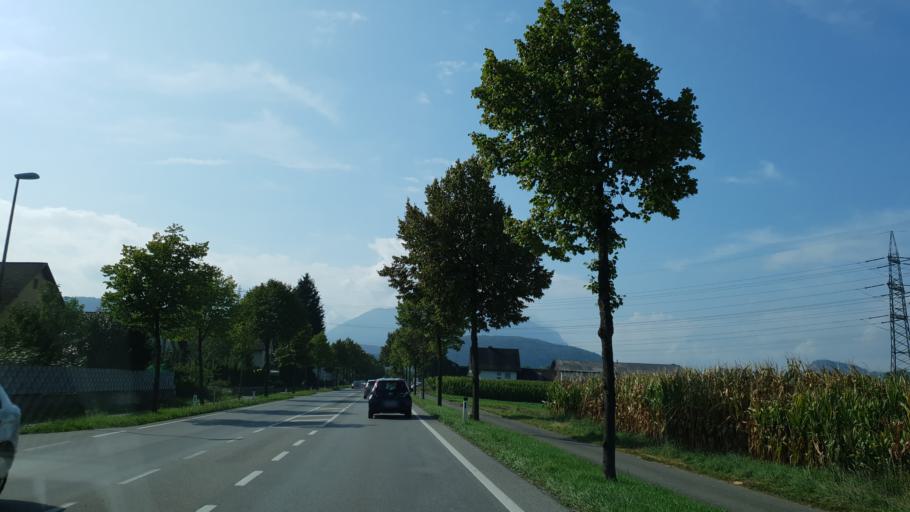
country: AT
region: Vorarlberg
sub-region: Politischer Bezirk Feldkirch
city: Rankweil
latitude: 47.2780
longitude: 9.6173
